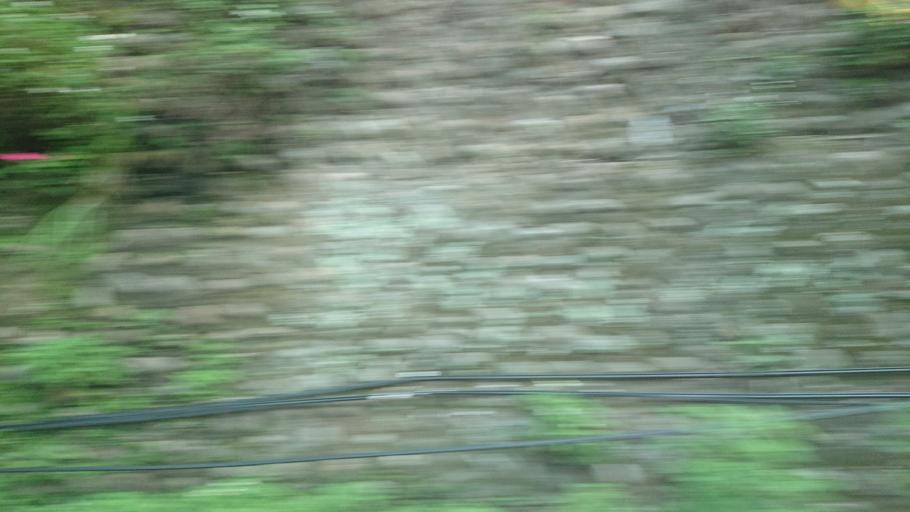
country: TW
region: Taiwan
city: Daxi
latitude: 24.8847
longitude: 121.3777
